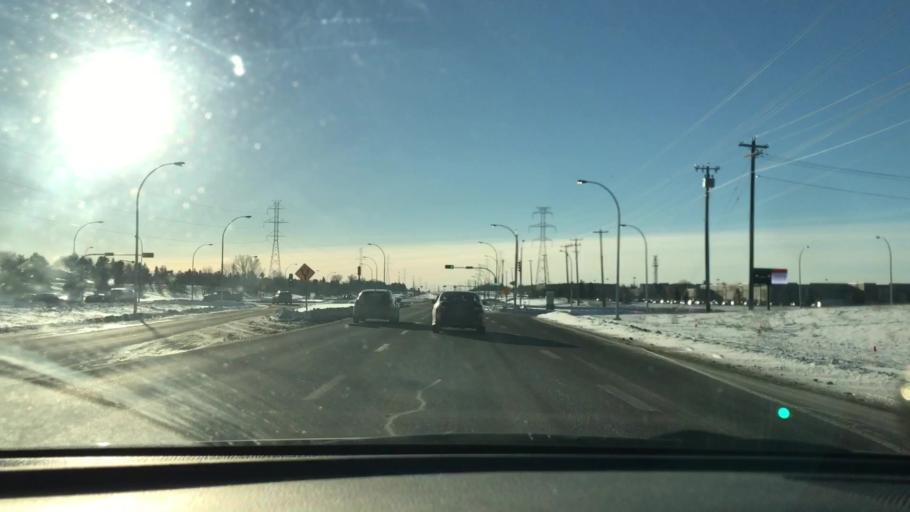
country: CA
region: Alberta
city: Edmonton
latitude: 53.4598
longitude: -113.4669
